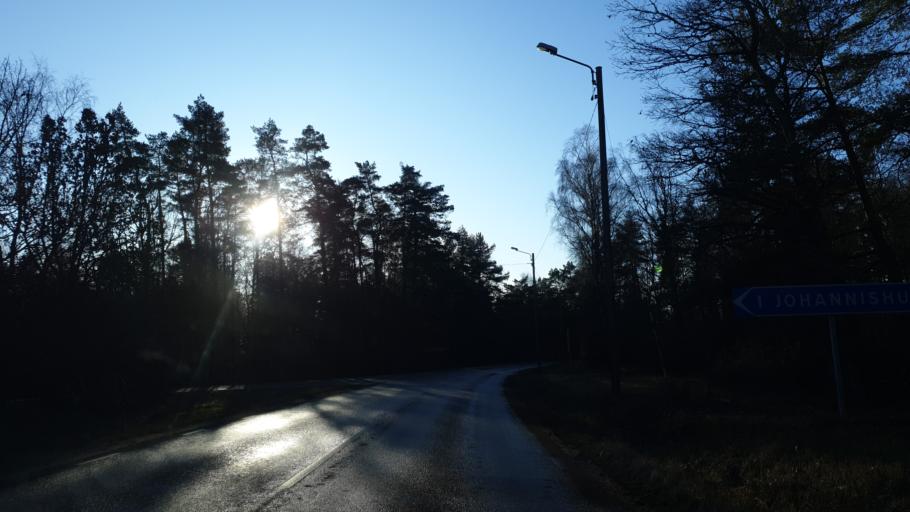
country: SE
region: Blekinge
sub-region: Karlskrona Kommun
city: Nattraby
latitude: 56.2221
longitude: 15.4058
